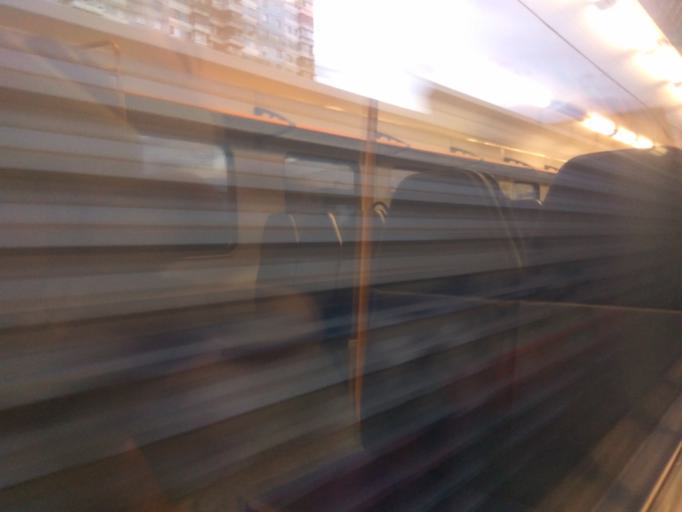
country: RU
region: Moscow
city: Solntsevo
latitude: 55.6497
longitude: 37.3804
